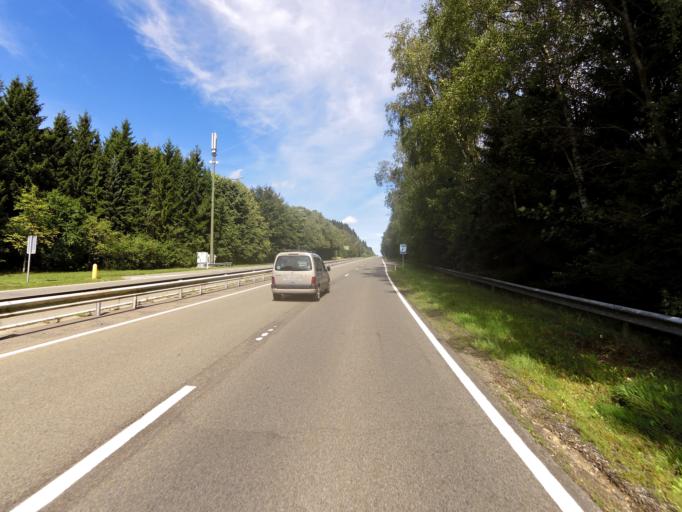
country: BE
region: Wallonia
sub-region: Province du Luxembourg
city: Saint-Hubert
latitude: 50.0369
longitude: 5.3866
